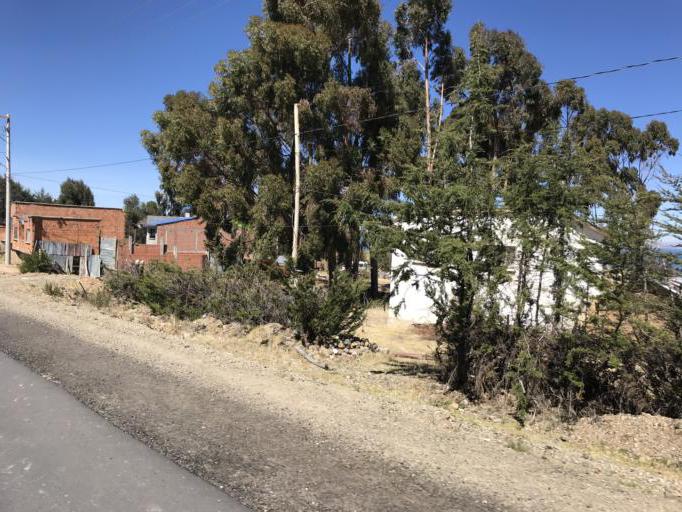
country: BO
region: La Paz
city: Huarina
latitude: -16.2142
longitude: -68.6572
